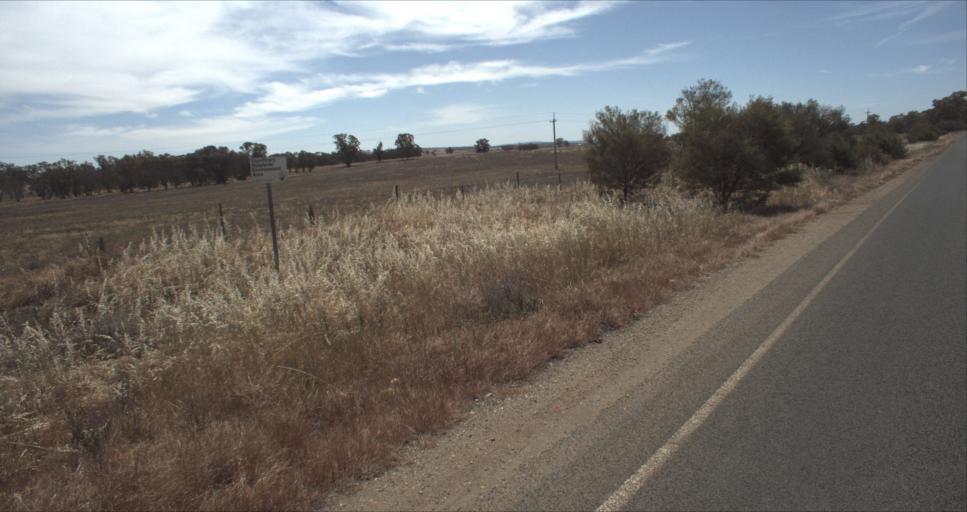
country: AU
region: New South Wales
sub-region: Leeton
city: Leeton
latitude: -34.6619
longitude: 146.4503
